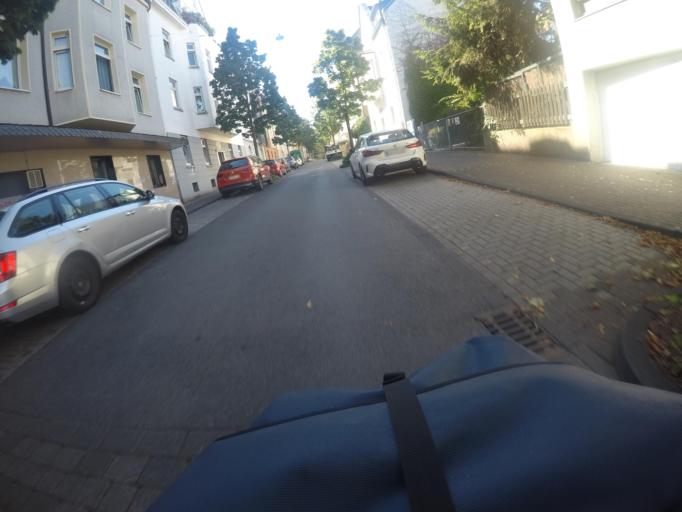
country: DE
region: North Rhine-Westphalia
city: Opladen
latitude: 51.0618
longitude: 7.0051
